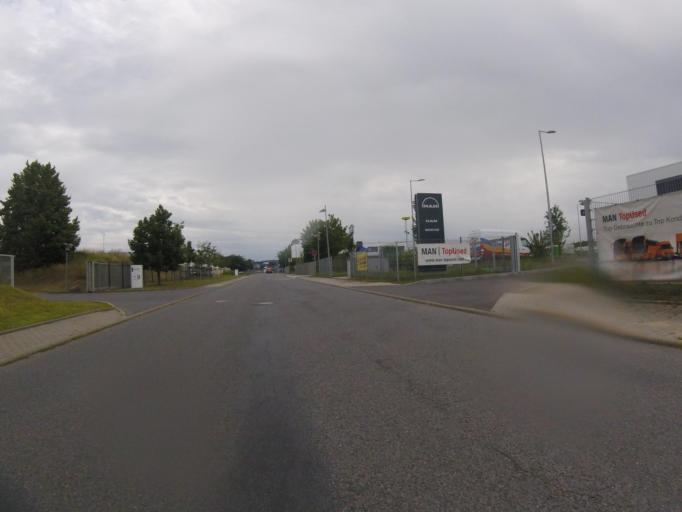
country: DE
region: Brandenburg
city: Wildau
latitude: 52.3210
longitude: 13.5933
